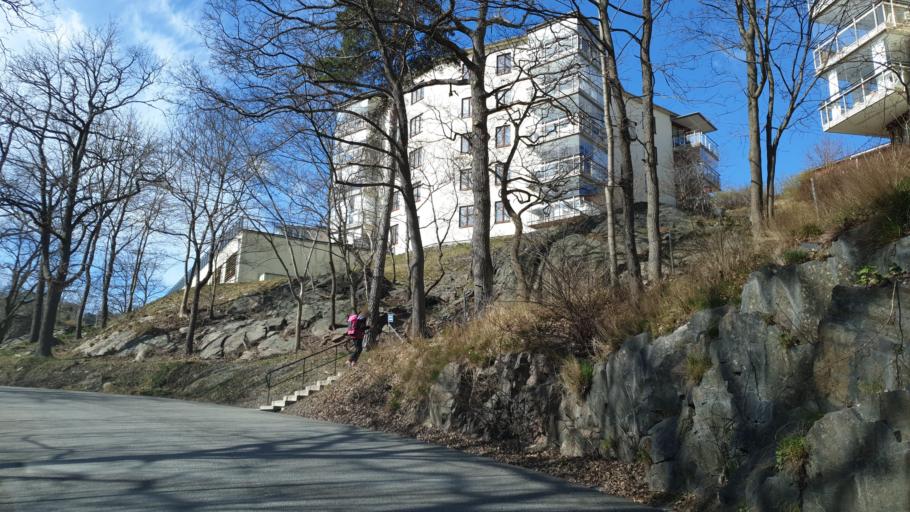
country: SE
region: Stockholm
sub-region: Nacka Kommun
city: Nacka
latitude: 59.3133
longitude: 18.1313
